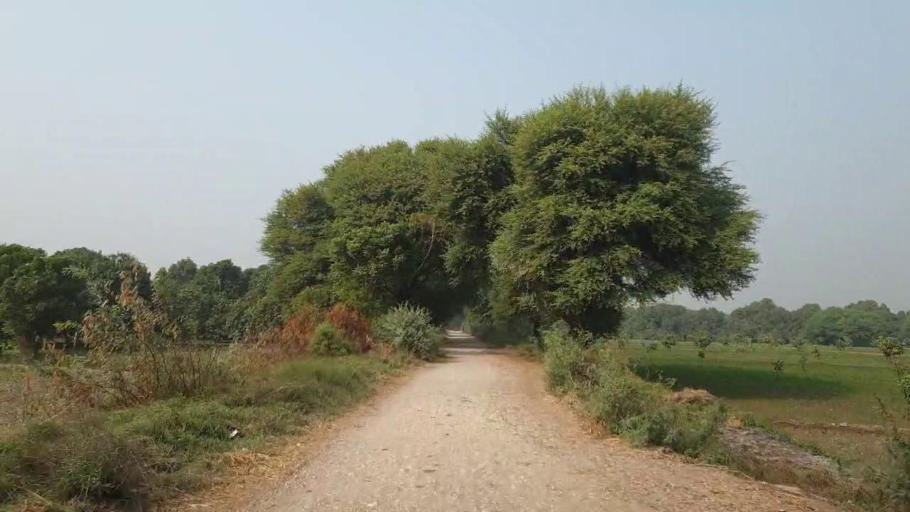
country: PK
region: Sindh
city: Tando Muhammad Khan
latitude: 25.2085
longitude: 68.5598
